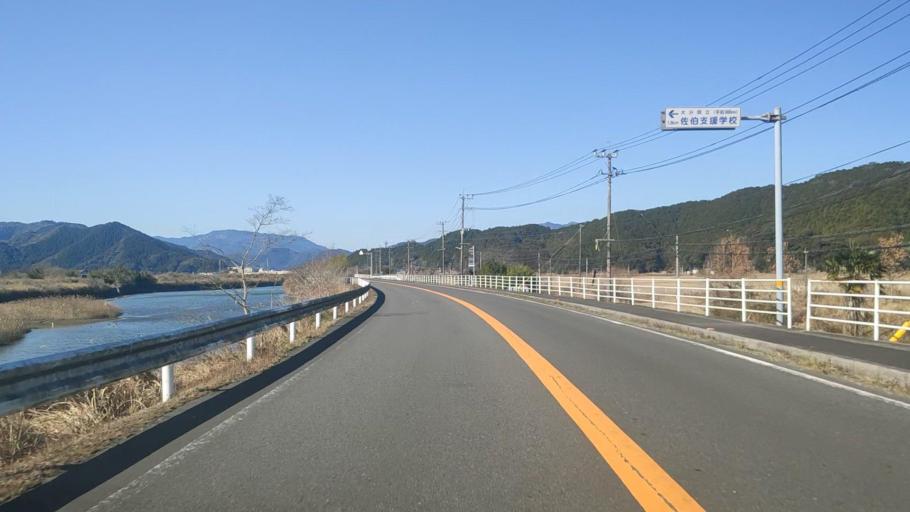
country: JP
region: Oita
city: Saiki
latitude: 32.9348
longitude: 131.9209
